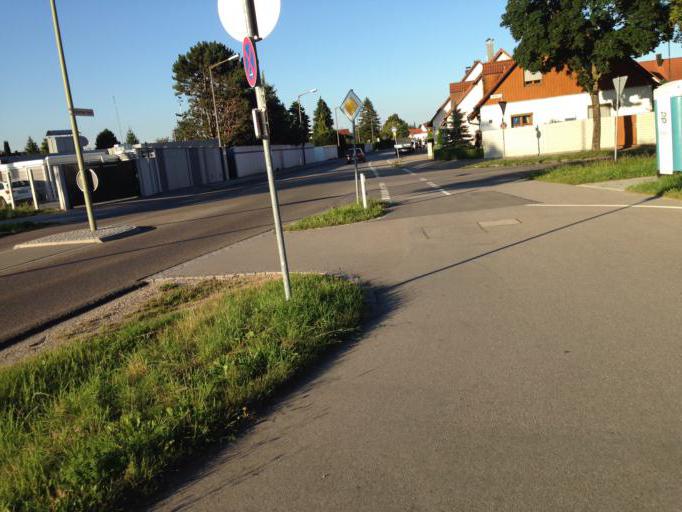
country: DE
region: Bavaria
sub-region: Swabia
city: Stadtbergen
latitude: 48.3538
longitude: 10.8569
